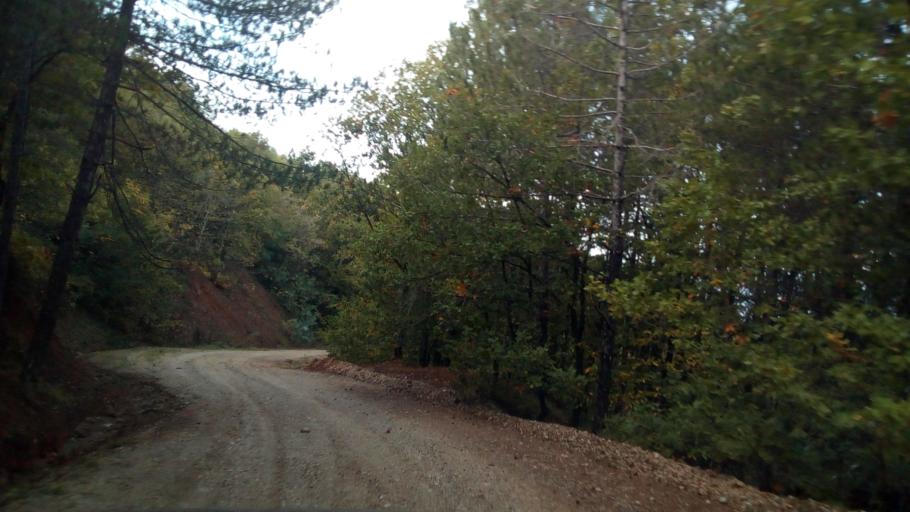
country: GR
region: West Greece
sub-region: Nomos Achaias
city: Kamarai
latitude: 38.4799
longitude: 22.0228
